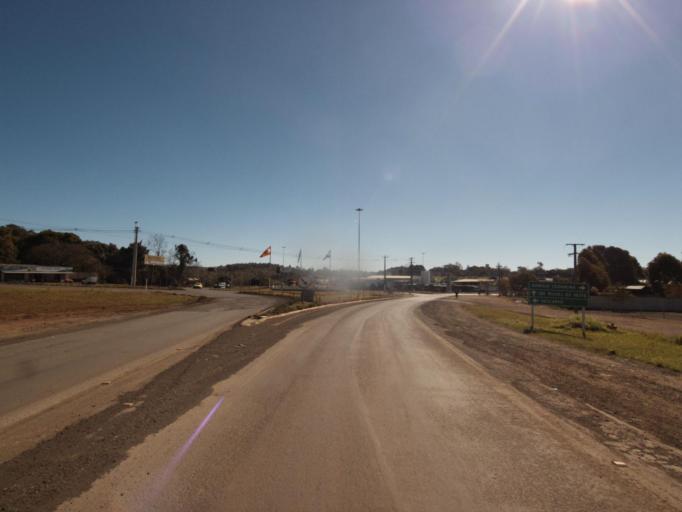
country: AR
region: Misiones
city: Bernardo de Irigoyen
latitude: -26.7618
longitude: -53.4996
